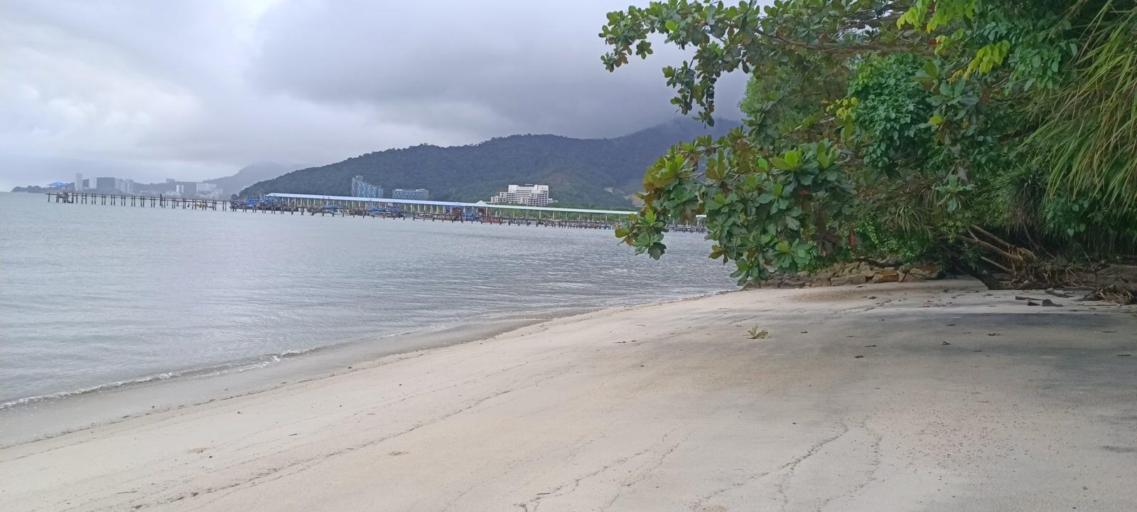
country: MY
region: Penang
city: Tanjung Tokong
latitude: 5.4619
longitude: 100.2040
